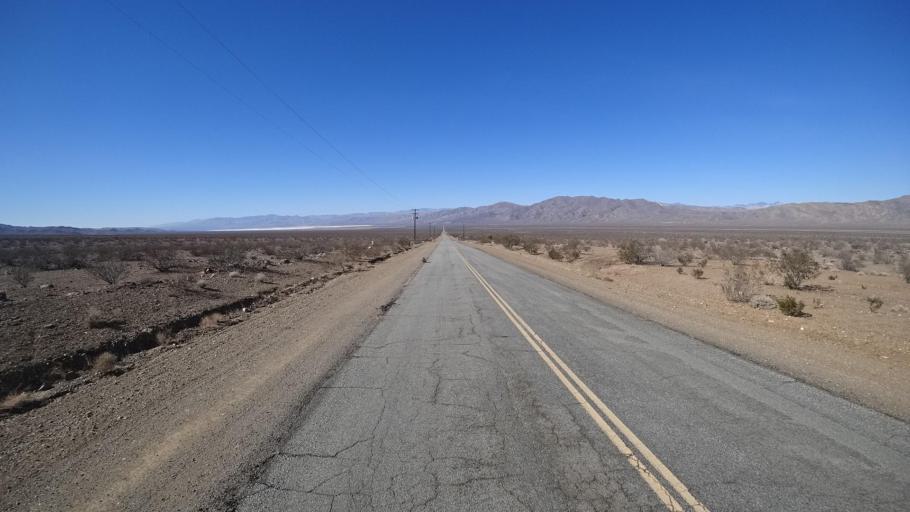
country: US
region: California
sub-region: Kern County
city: Ridgecrest
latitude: 35.3820
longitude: -117.6933
